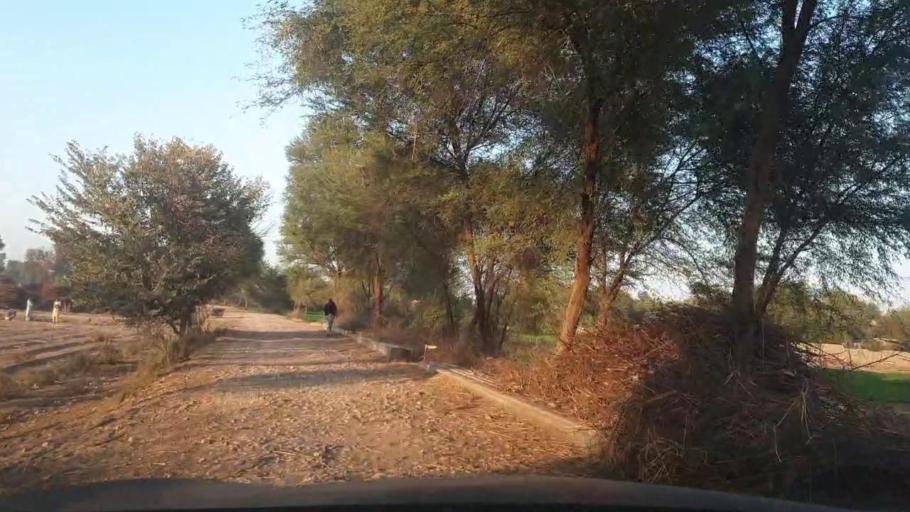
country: PK
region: Sindh
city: Ubauro
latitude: 28.1782
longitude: 69.6041
